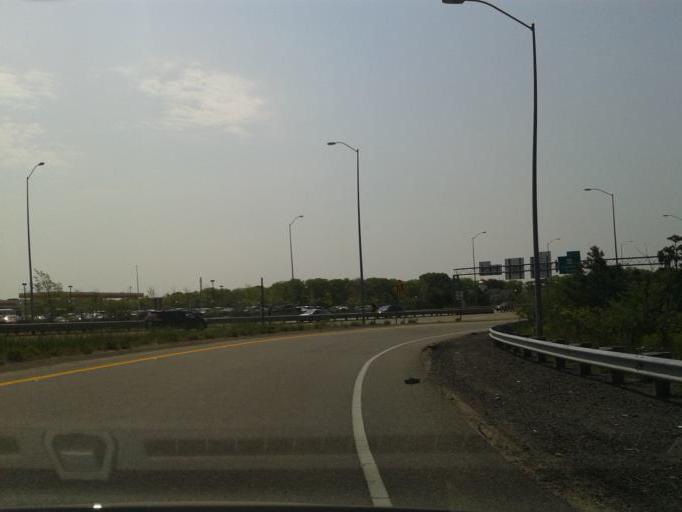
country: US
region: Massachusetts
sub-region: Barnstable County
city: Sagamore
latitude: 41.7814
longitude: -70.5440
